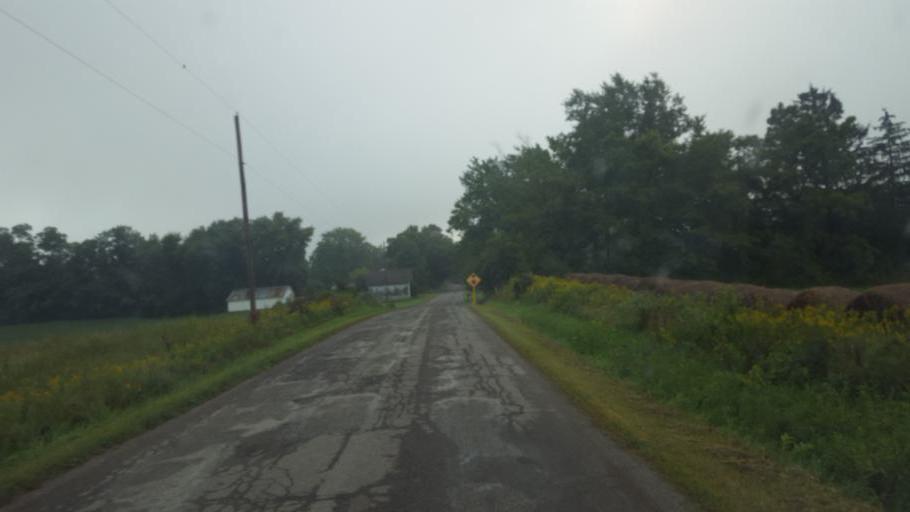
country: US
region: Ohio
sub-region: Morrow County
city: Mount Gilead
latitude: 40.5340
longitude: -82.7138
